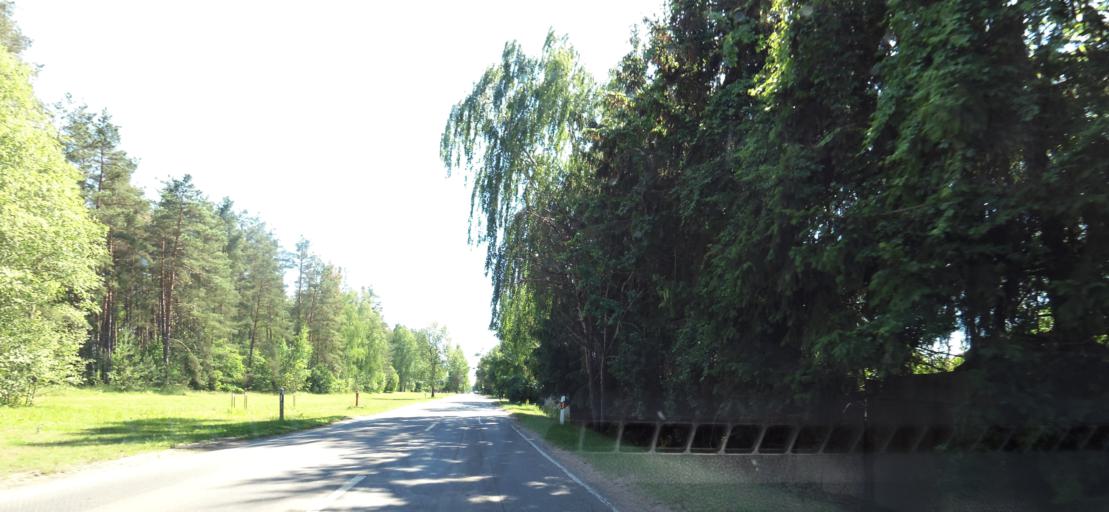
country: LT
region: Vilnius County
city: Rasos
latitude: 54.7890
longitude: 25.3502
